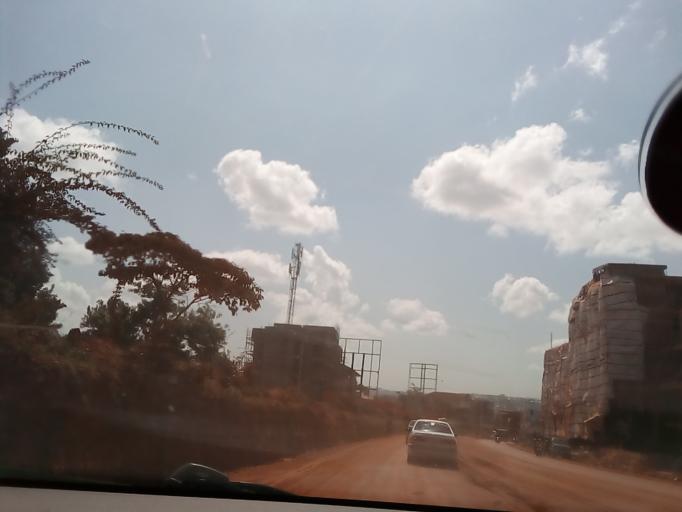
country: UG
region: Central Region
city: Masaka
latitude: -0.3349
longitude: 31.7412
